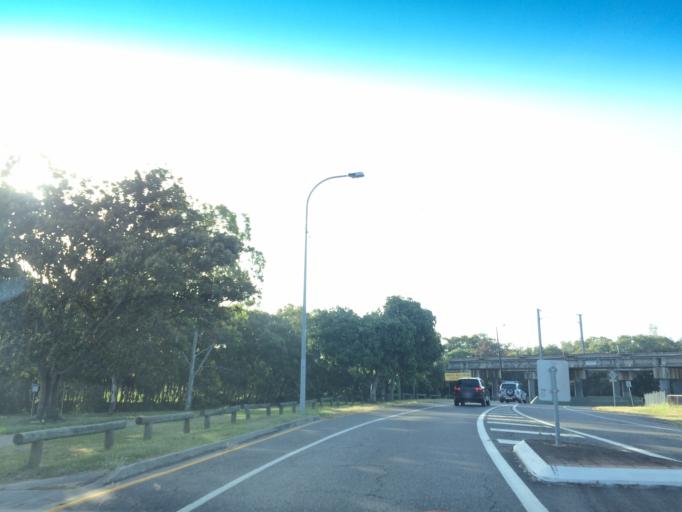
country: AU
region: Queensland
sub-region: Brisbane
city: Greenslopes
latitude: -27.4947
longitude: 153.0489
